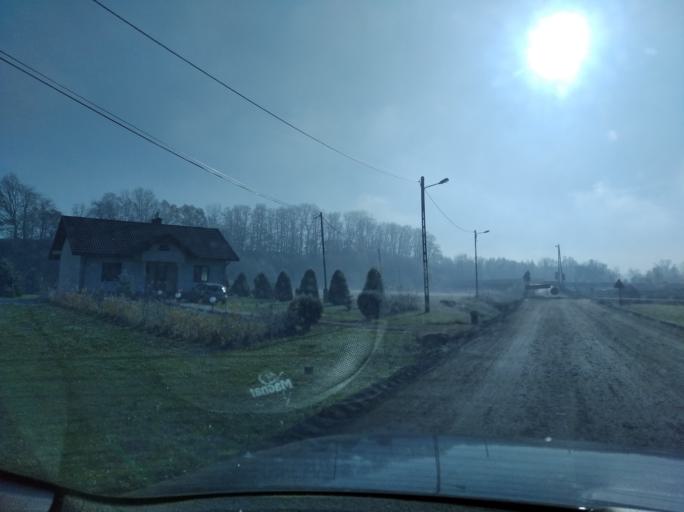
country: PL
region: Subcarpathian Voivodeship
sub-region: Powiat strzyzowski
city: Wysoka Strzyzowska
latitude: 49.8662
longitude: 21.7067
